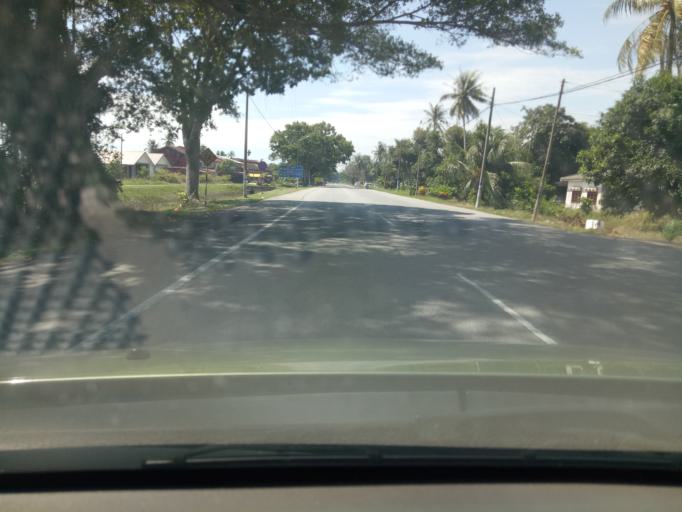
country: MY
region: Kedah
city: Gurun
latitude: 5.9279
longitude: 100.4189
